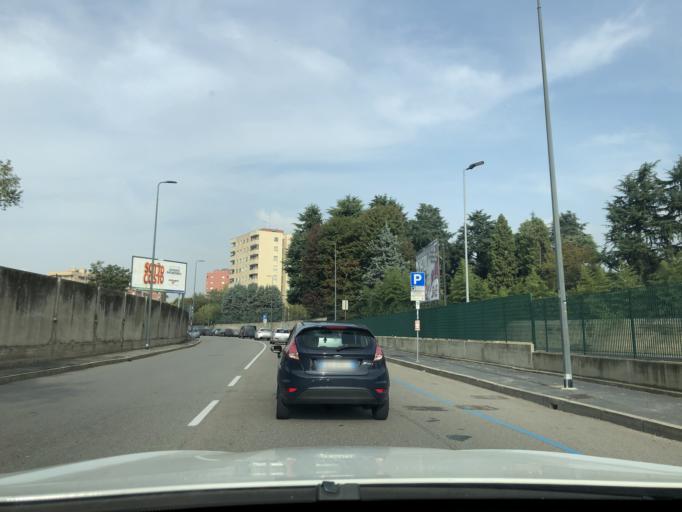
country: IT
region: Lombardy
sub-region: Citta metropolitana di Milano
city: Pero
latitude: 45.4861
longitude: 9.1184
